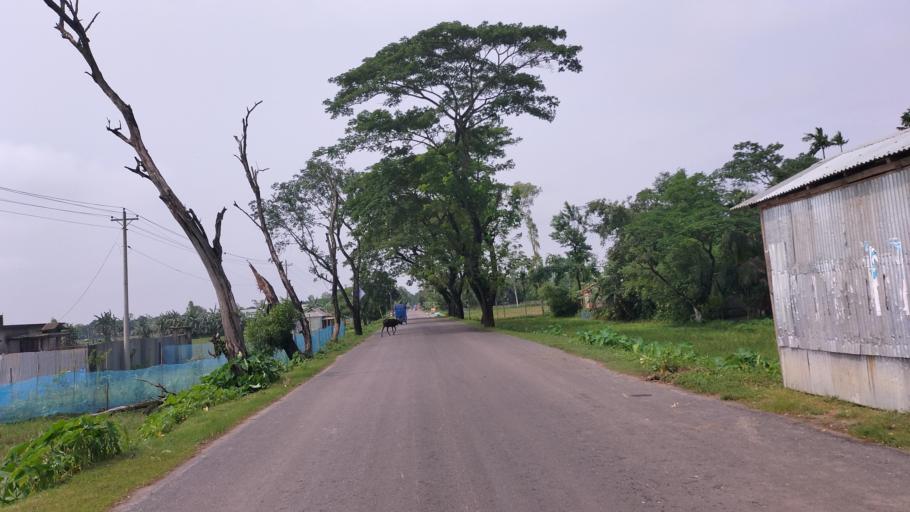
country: BD
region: Dhaka
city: Netrakona
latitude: 24.9474
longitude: 90.8317
